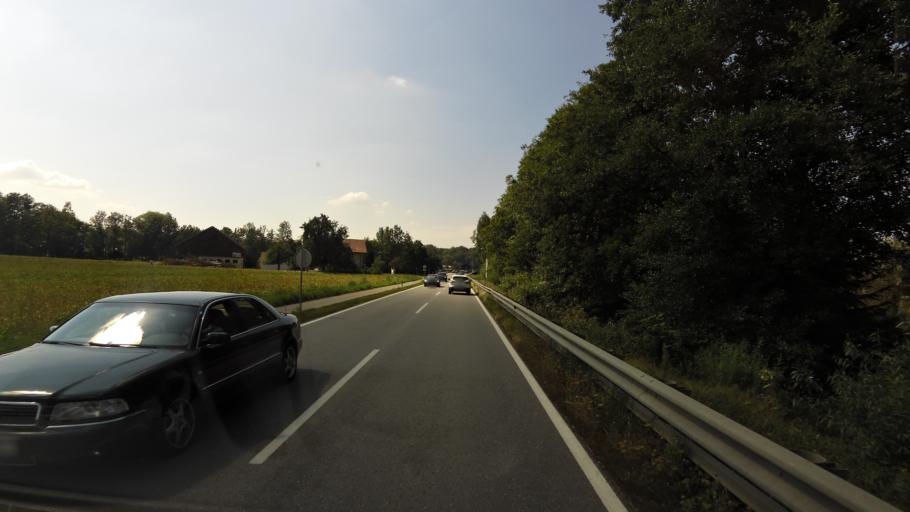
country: AT
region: Upper Austria
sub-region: Politischer Bezirk Braunau am Inn
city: Braunau am Inn
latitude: 48.1464
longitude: 13.1284
